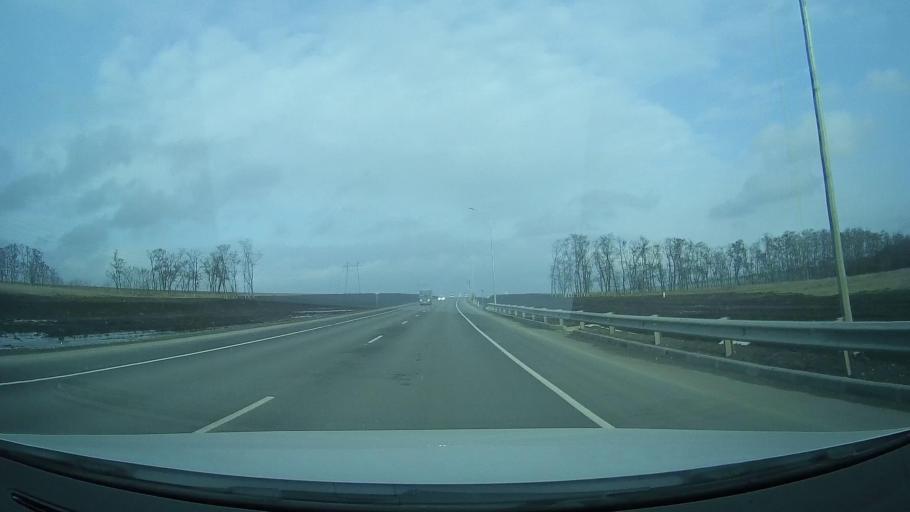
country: RU
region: Rostov
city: Grushevskaya
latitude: 47.3864
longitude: 39.8460
